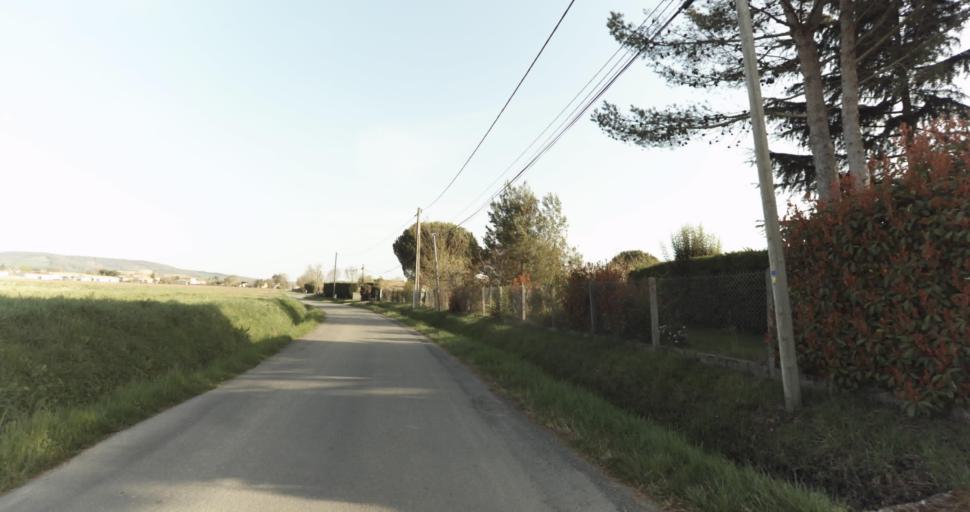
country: FR
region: Midi-Pyrenees
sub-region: Departement du Tarn
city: Saint-Sulpice-la-Pointe
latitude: 43.7600
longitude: 1.6781
